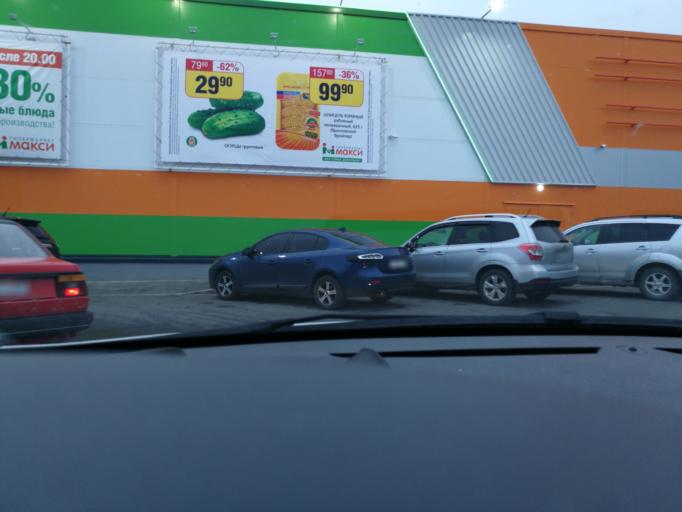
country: RU
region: Arkhangelskaya
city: Severodvinsk
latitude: 64.5573
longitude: 39.7761
